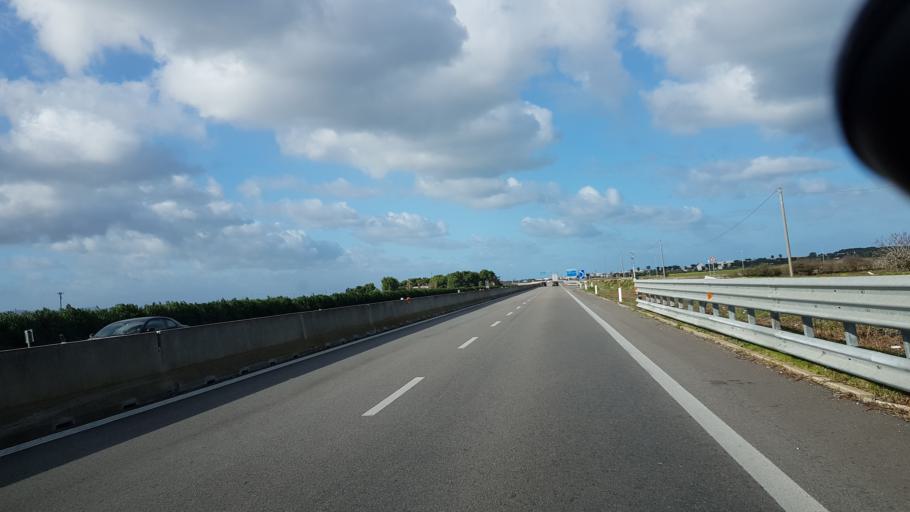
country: IT
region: Apulia
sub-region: Provincia di Brindisi
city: Carovigno
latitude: 40.7475
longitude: 17.7064
